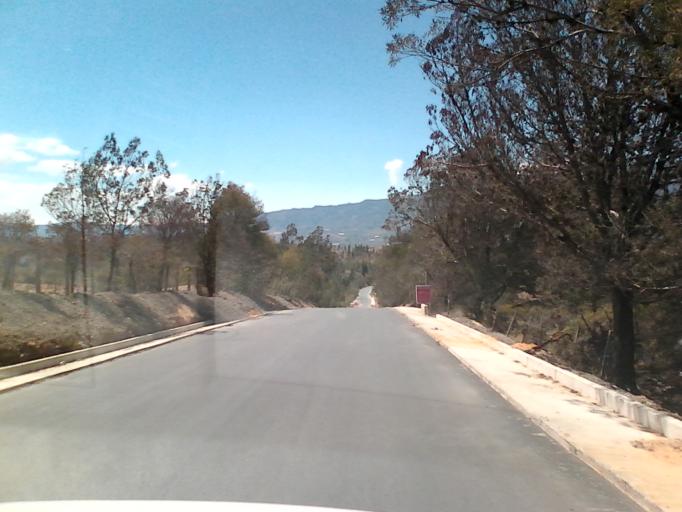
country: CO
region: Boyaca
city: Villa de Leiva
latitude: 5.6234
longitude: -73.5761
